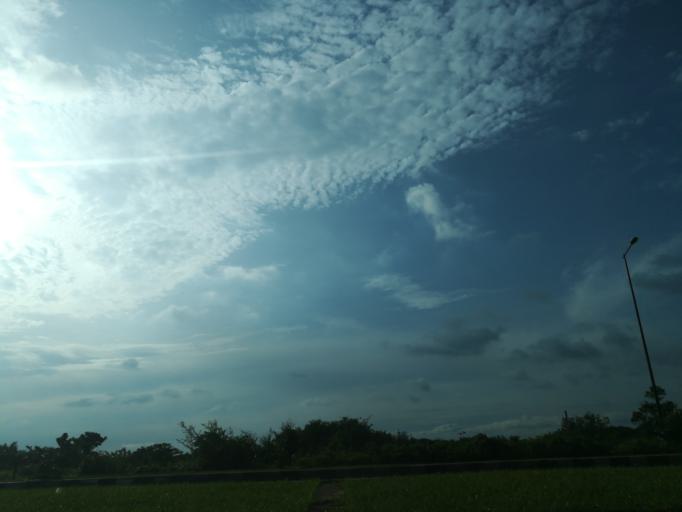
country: NG
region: Lagos
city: Ebute Ikorodu
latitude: 6.6178
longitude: 3.4480
